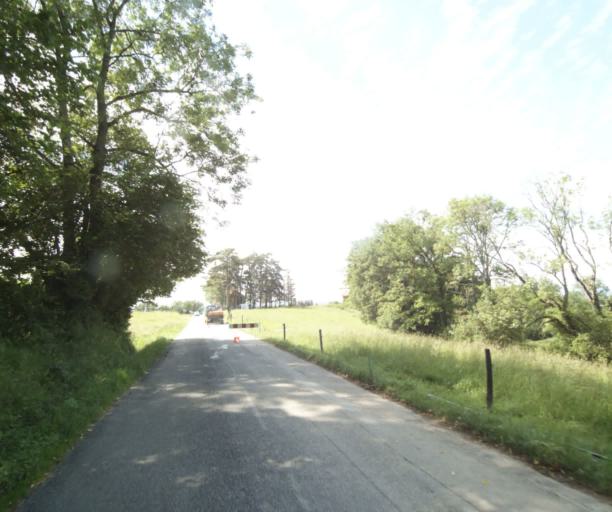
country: FR
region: Rhone-Alpes
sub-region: Departement de la Haute-Savoie
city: Bons-en-Chablais
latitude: 46.2780
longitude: 6.4186
